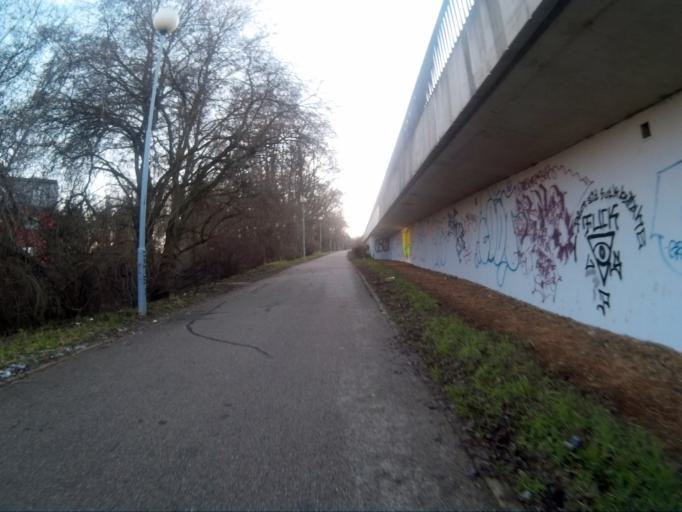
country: CZ
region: South Moravian
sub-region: Mesto Brno
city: Brno
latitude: 49.1756
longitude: 16.5946
